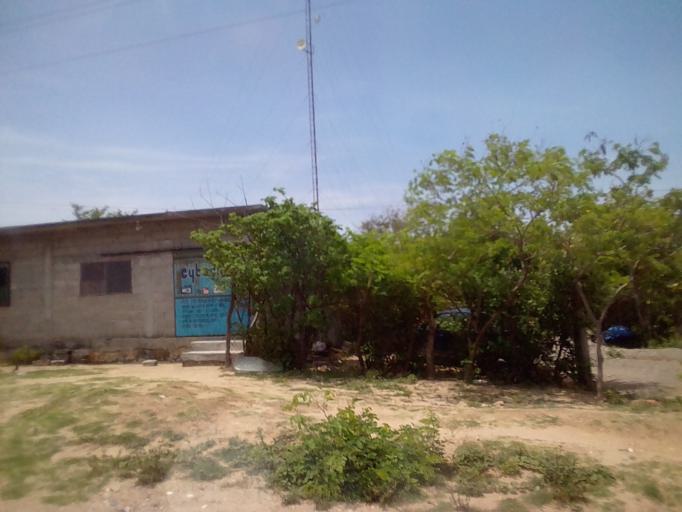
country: MX
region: Oaxaca
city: San Mateo del Mar
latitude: 16.2093
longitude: -94.9942
